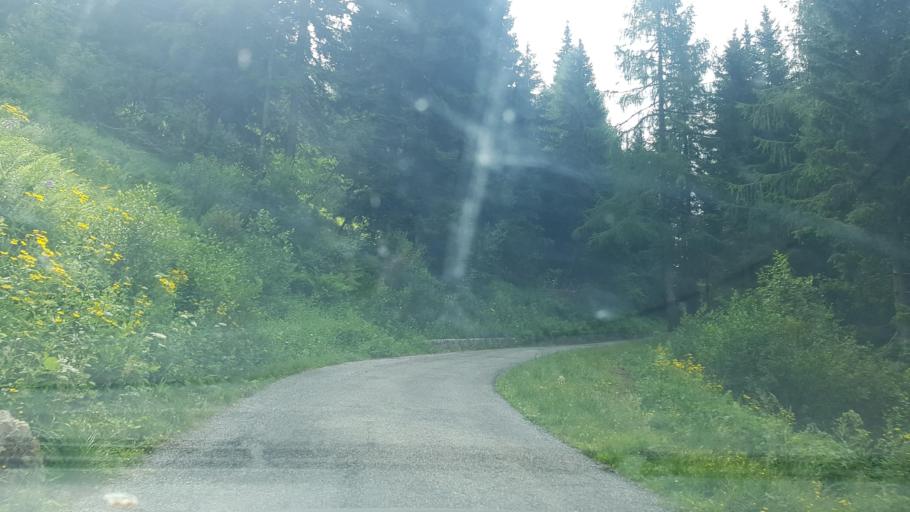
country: IT
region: Friuli Venezia Giulia
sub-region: Provincia di Udine
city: Paularo
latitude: 46.5724
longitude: 13.1631
